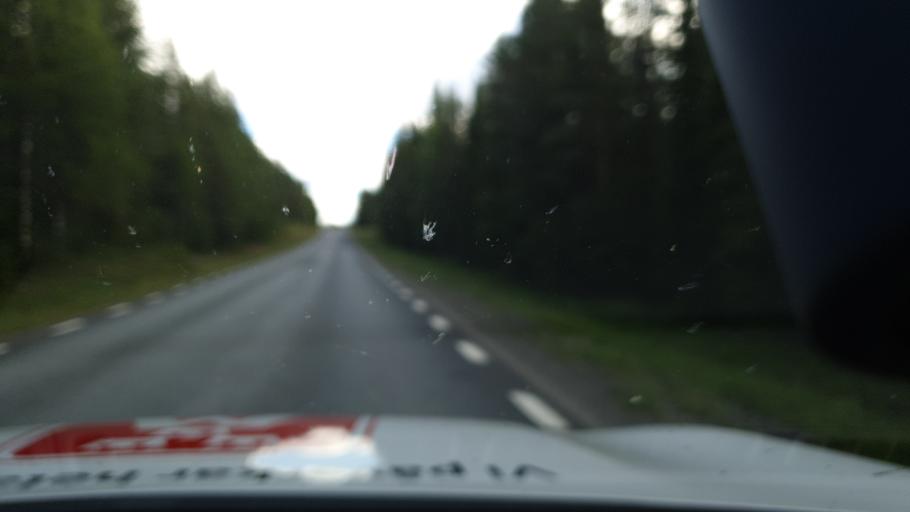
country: SE
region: Vaesterbotten
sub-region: Mala Kommun
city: Mala
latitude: 65.1492
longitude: 18.6295
